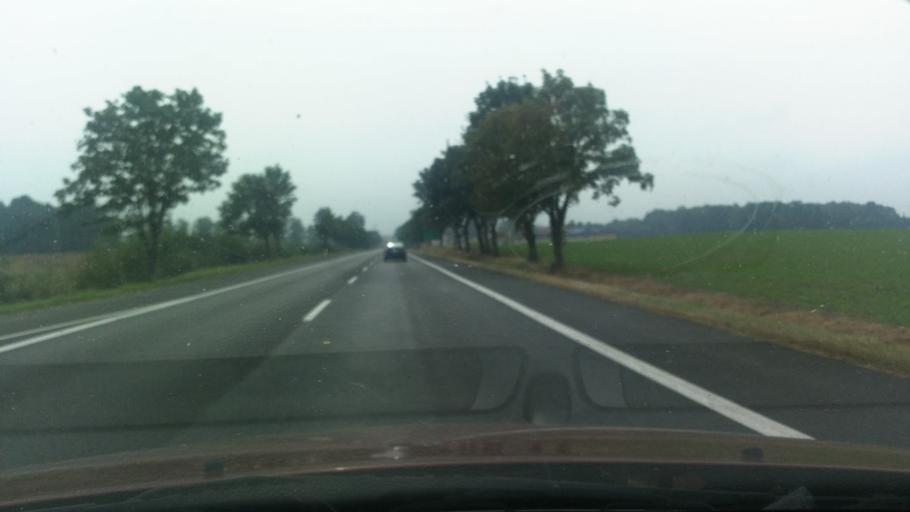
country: PL
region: Lower Silesian Voivodeship
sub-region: Powiat zgorzelecki
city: Lagow
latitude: 51.1673
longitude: 15.0297
